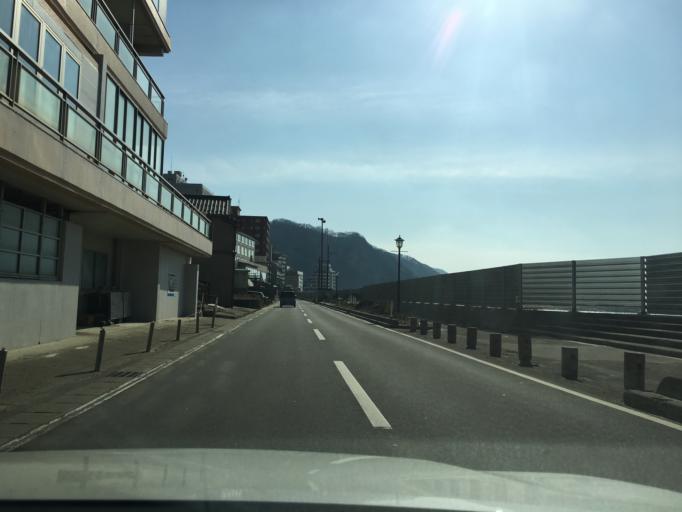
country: JP
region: Yamagata
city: Tsuruoka
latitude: 38.7827
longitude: 139.7526
